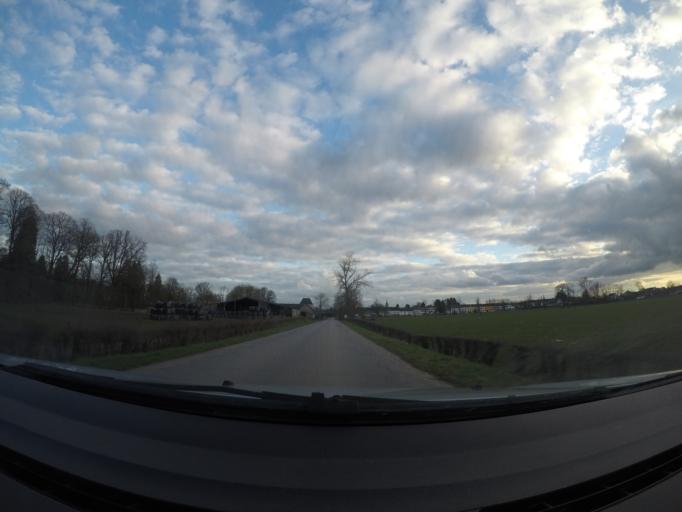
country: BE
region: Wallonia
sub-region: Province du Luxembourg
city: Etalle
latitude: 49.6778
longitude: 5.5654
